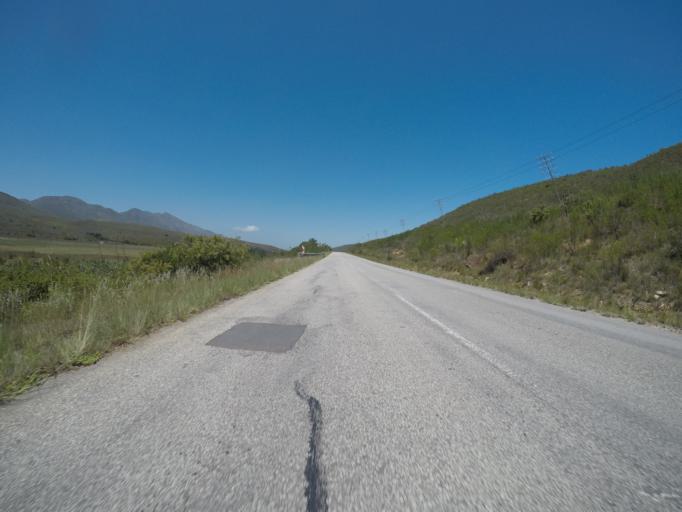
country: ZA
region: Eastern Cape
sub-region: Cacadu District Municipality
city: Kareedouw
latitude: -33.8984
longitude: 24.1208
